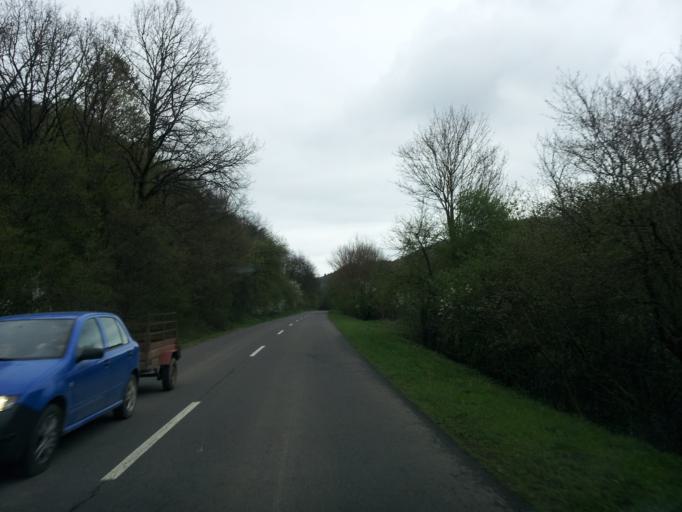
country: HU
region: Borsod-Abauj-Zemplen
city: Rudabanya
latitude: 48.4788
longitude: 20.6022
